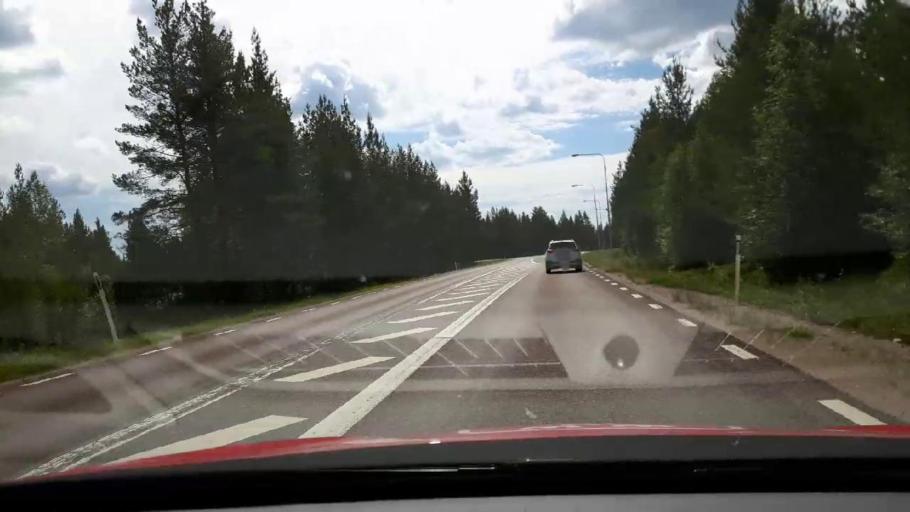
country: SE
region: Jaemtland
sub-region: Harjedalens Kommun
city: Sveg
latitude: 62.1308
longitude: 14.9717
